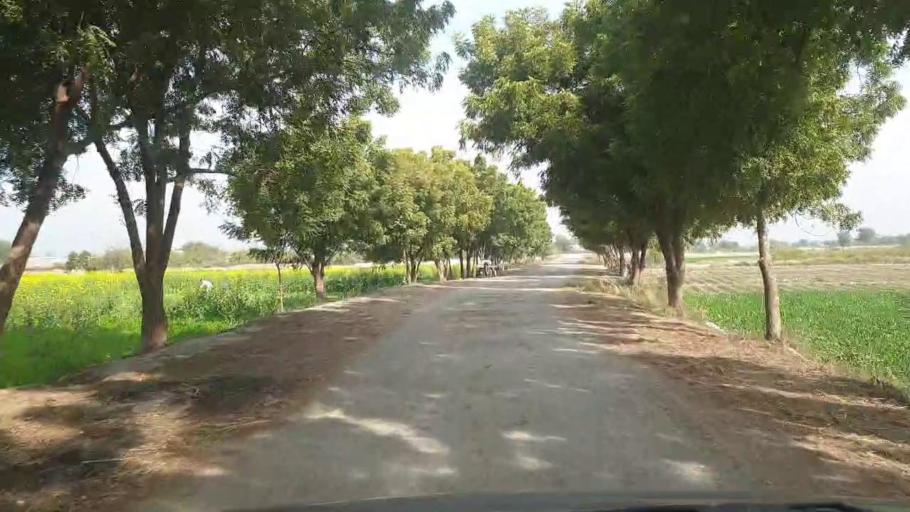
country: PK
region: Sindh
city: Khadro
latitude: 26.1554
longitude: 68.6952
